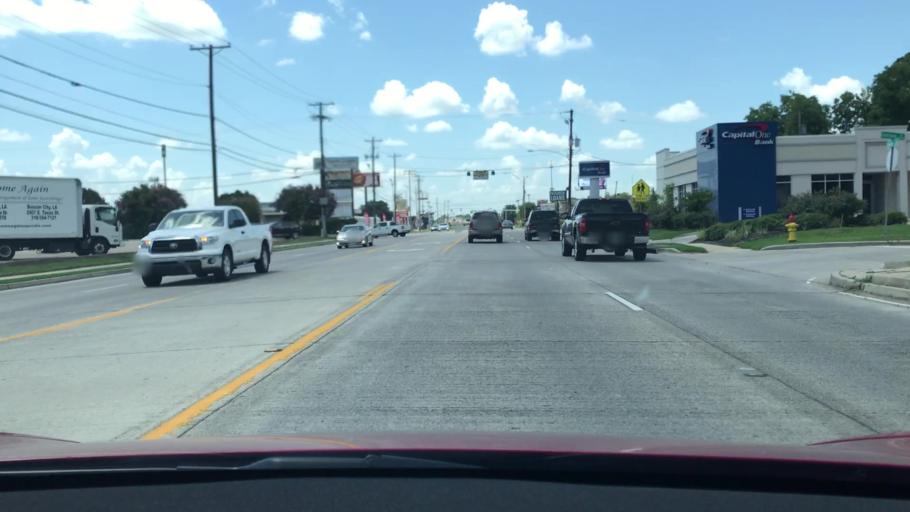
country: US
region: Louisiana
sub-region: Bossier Parish
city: Bossier City
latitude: 32.4556
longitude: -93.7222
